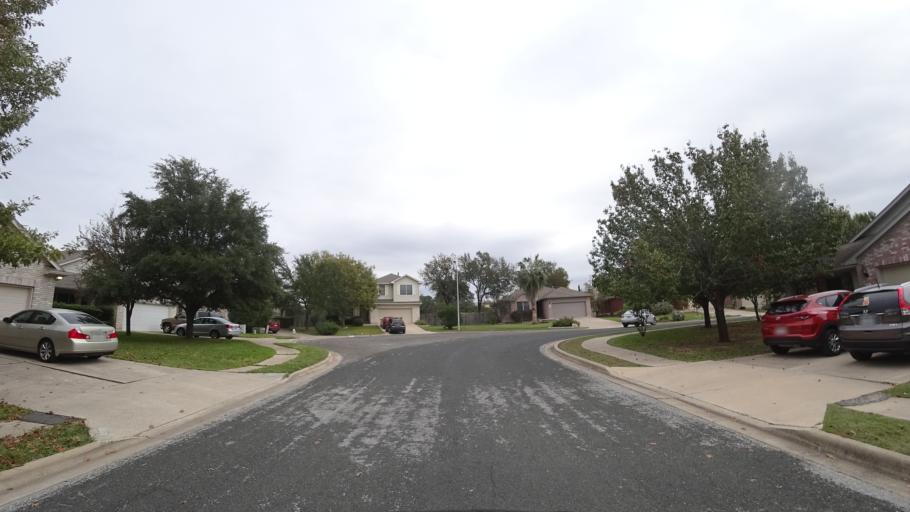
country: US
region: Texas
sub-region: Travis County
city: Shady Hollow
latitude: 30.1531
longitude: -97.8498
